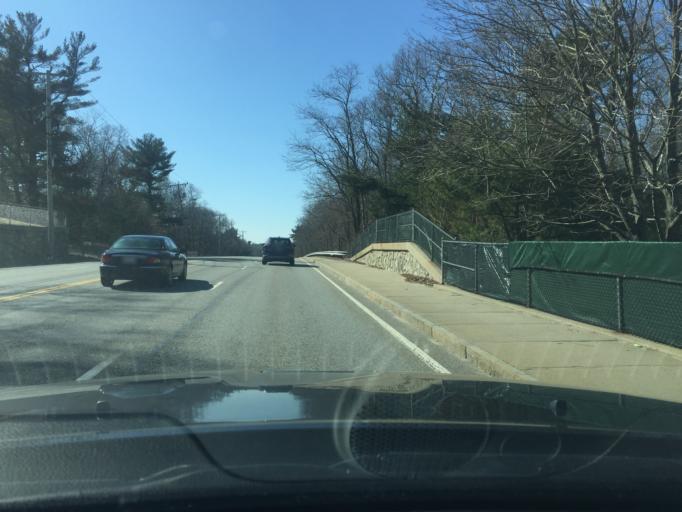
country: US
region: Massachusetts
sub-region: Plymouth County
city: North Plymouth
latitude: 41.9481
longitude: -70.6970
